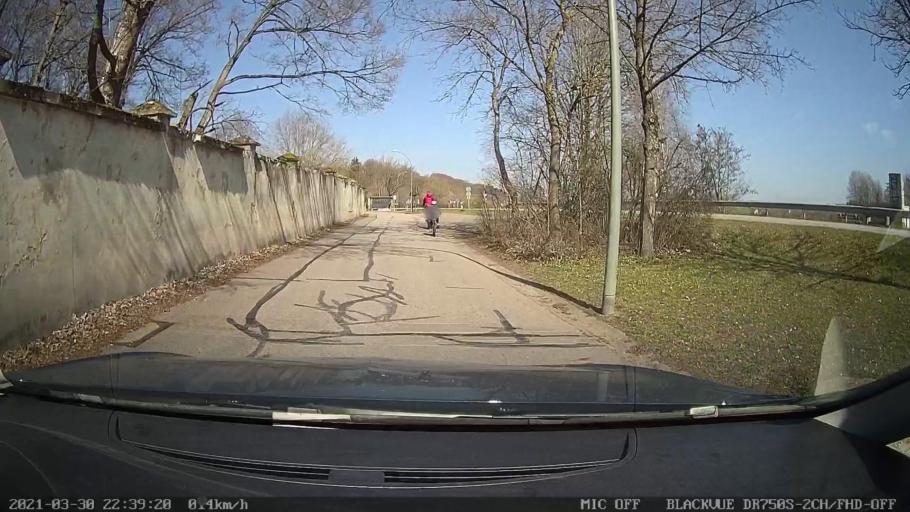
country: DE
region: Bavaria
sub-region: Upper Palatinate
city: Zeitlarn
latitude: 49.0920
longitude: 12.1090
